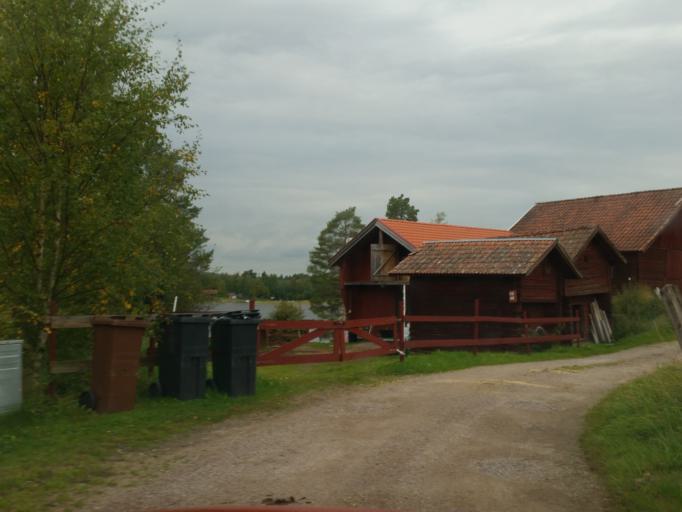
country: SE
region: Dalarna
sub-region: Leksand Municipality
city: Smedby
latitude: 60.6818
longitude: 15.1349
